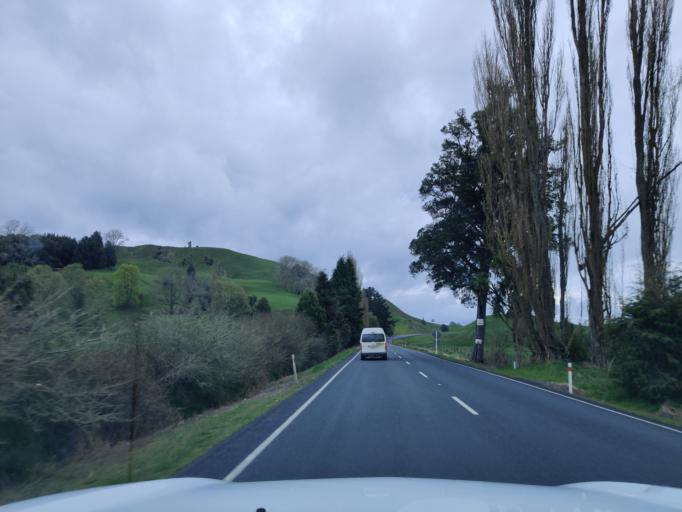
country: NZ
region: Waikato
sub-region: Otorohanga District
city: Otorohanga
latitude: -38.4722
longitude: 175.1730
